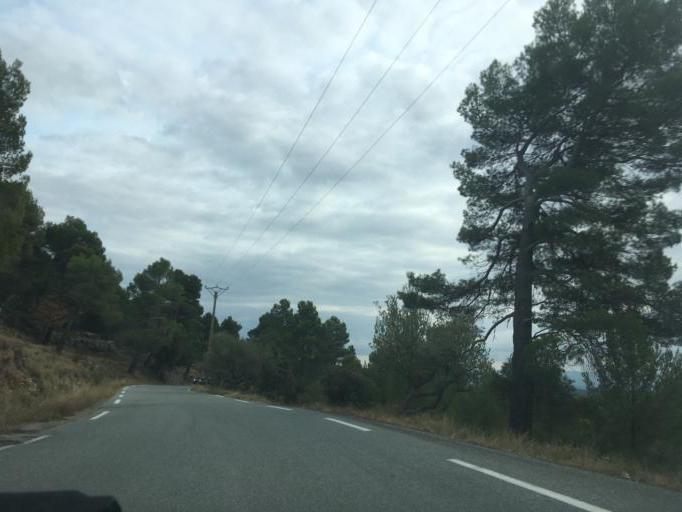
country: FR
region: Provence-Alpes-Cote d'Azur
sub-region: Departement du Var
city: Villecroze
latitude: 43.5766
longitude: 6.3163
